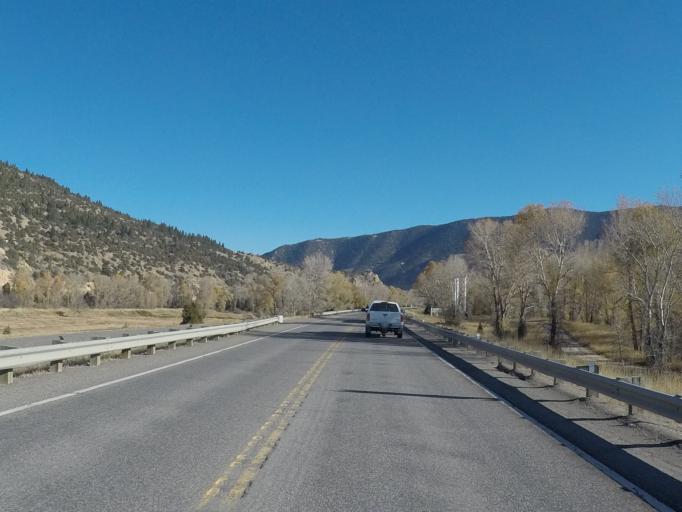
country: US
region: Montana
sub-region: Park County
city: Livingston
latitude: 45.5754
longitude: -110.5860
